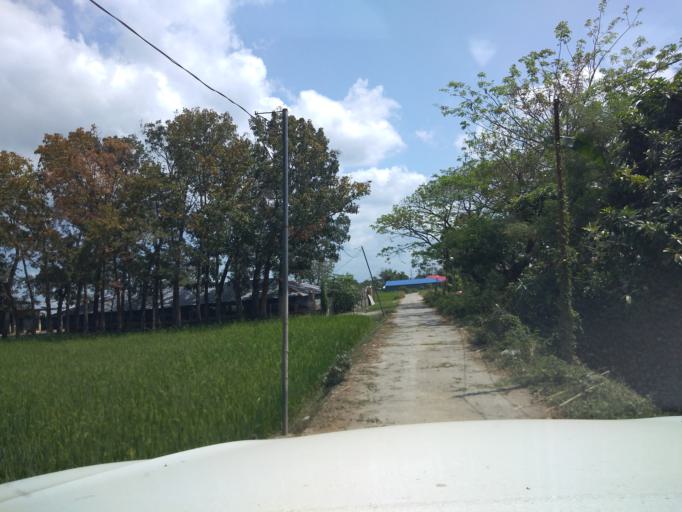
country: PH
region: Central Luzon
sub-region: Province of Pampanga
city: Lourdes
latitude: 15.0197
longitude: 120.8543
